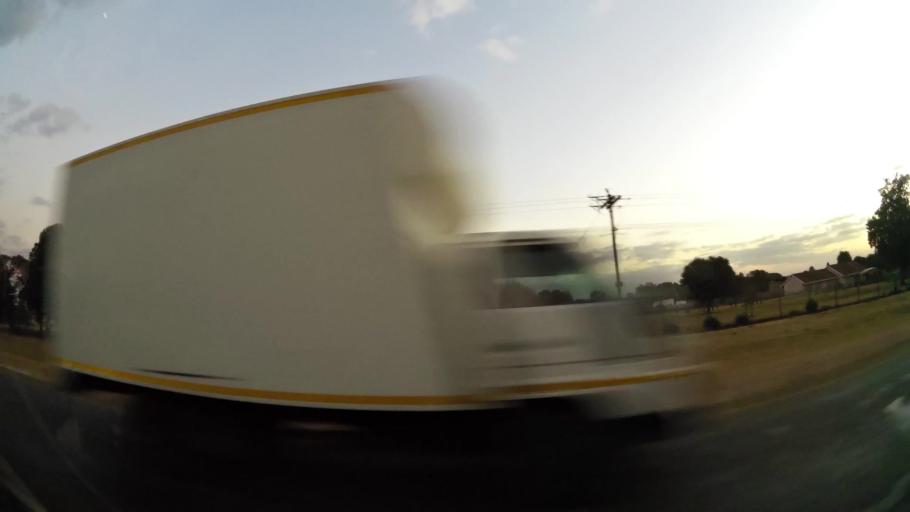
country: ZA
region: Gauteng
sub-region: West Rand District Municipality
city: Randfontein
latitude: -26.0927
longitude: 27.6764
